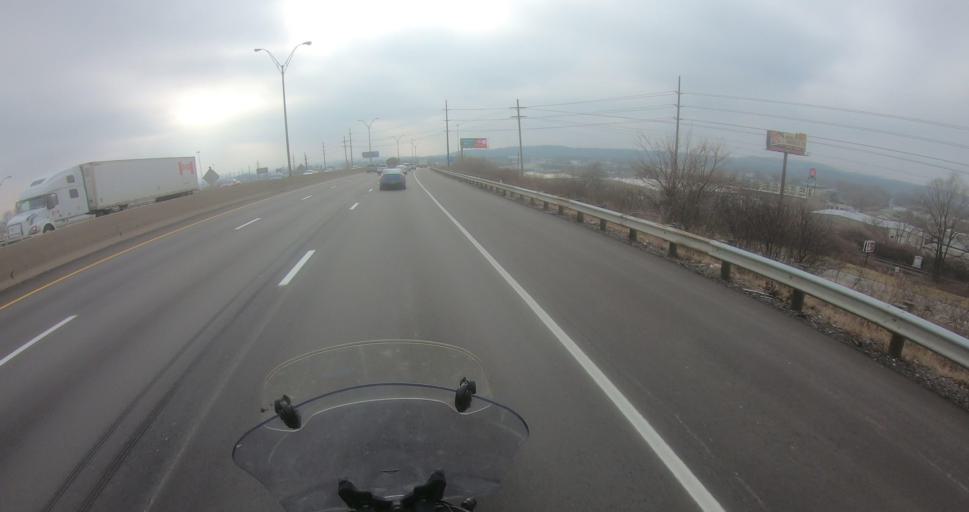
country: US
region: Ohio
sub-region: Montgomery County
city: Moraine
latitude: 39.7207
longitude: -84.2140
